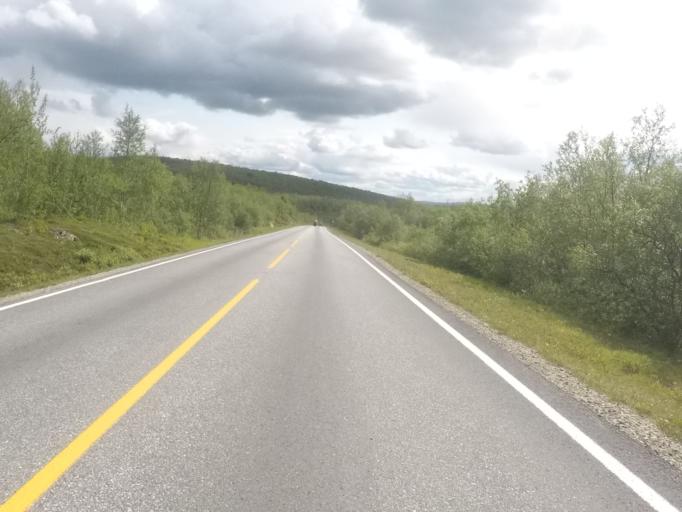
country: NO
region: Finnmark Fylke
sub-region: Karasjok
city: Karasjohka
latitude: 69.5117
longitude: 25.4665
